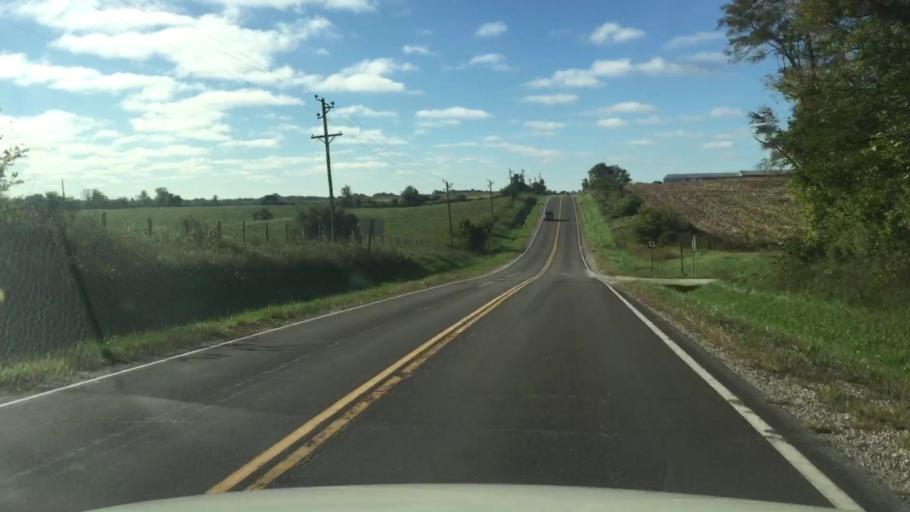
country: US
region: Missouri
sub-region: Howard County
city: New Franklin
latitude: 39.0793
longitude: -92.7456
